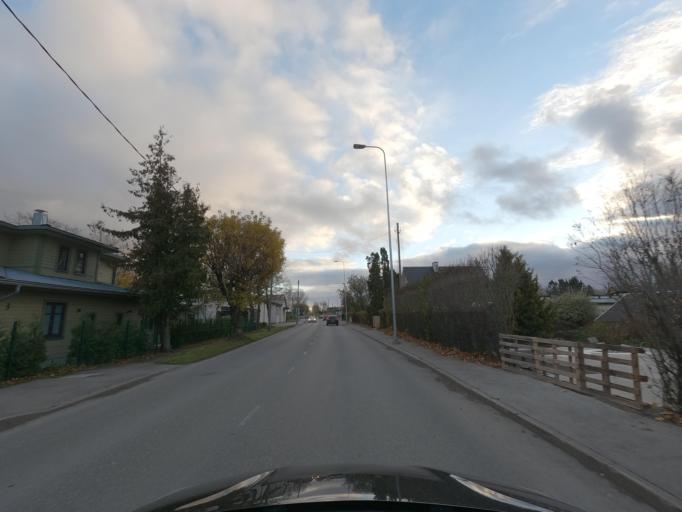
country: EE
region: Harju
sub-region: Keila linn
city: Keila
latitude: 59.3073
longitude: 24.4254
